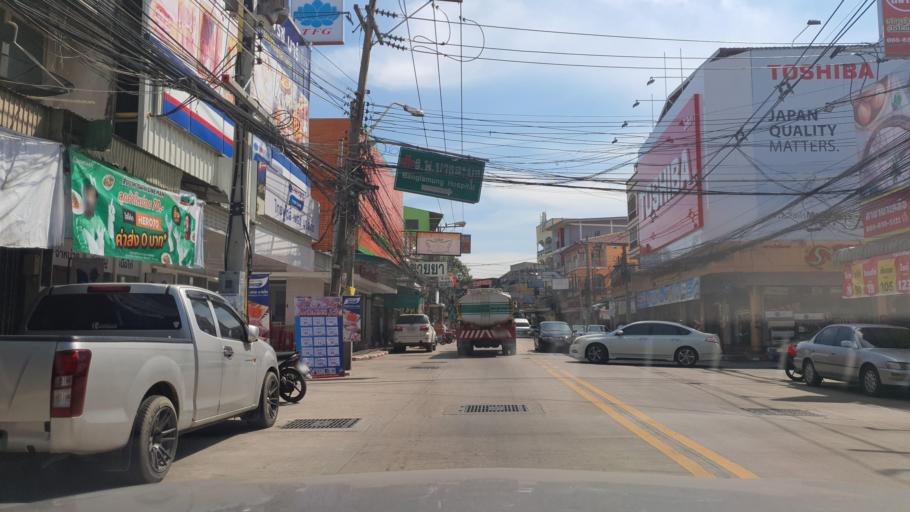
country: TH
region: Chon Buri
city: Phatthaya
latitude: 12.9696
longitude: 100.9077
